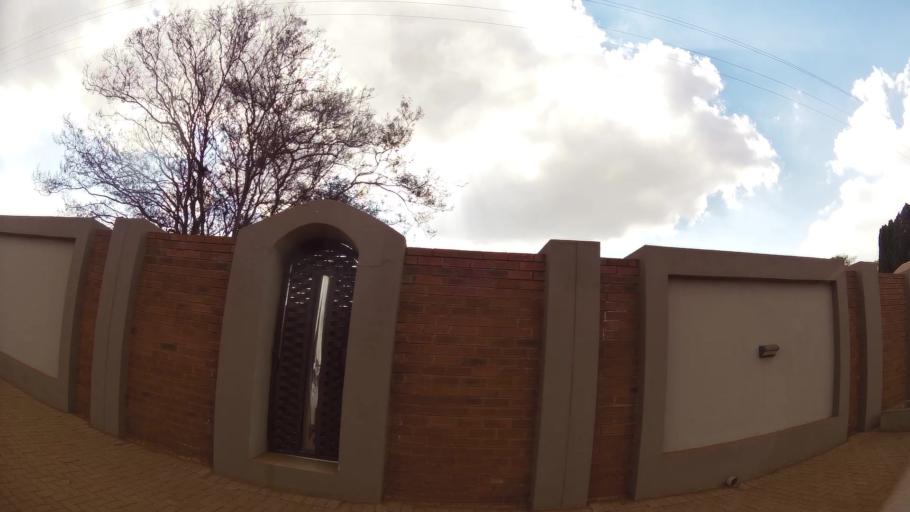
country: ZA
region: Mpumalanga
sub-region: Nkangala District Municipality
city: Delmas
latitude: -26.1310
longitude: 28.6731
